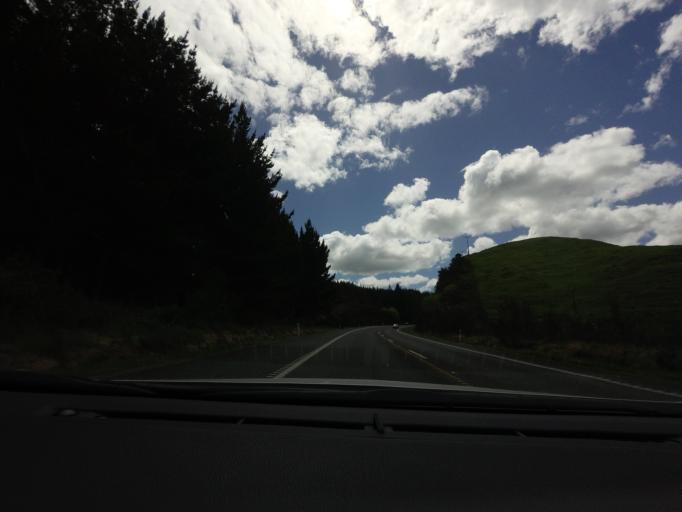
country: NZ
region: Bay of Plenty
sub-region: Rotorua District
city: Rotorua
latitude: -38.2874
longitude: 176.3495
